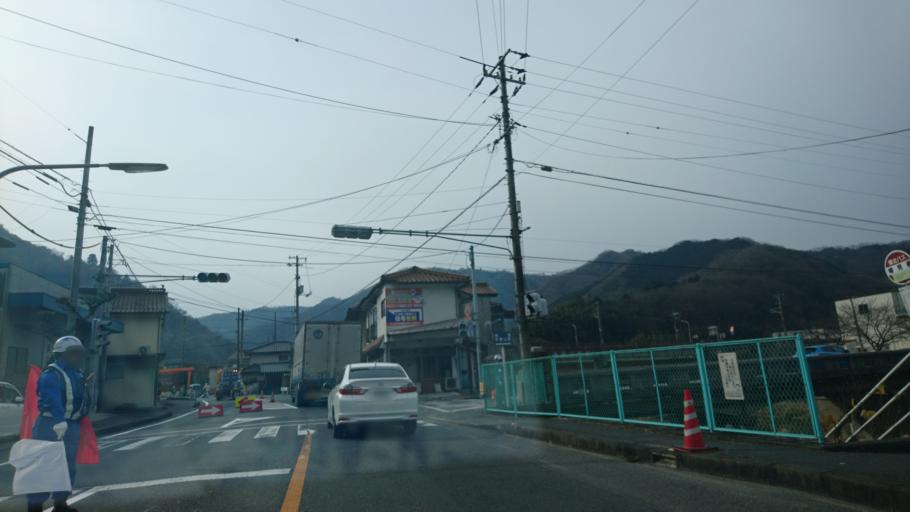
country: JP
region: Okayama
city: Takahashi
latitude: 34.8244
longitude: 133.6201
